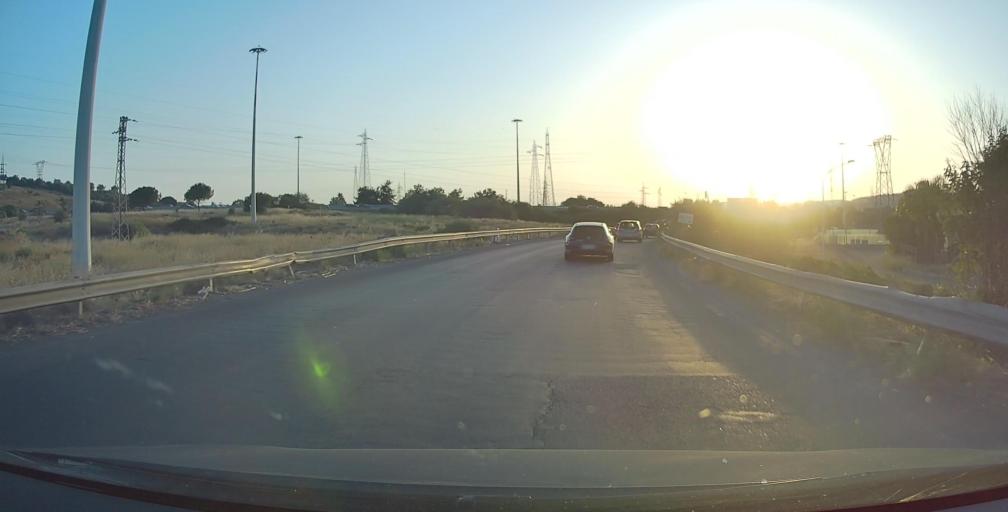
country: IT
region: Sicily
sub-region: Catania
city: Misterbianco
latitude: 37.5084
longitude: 15.0219
